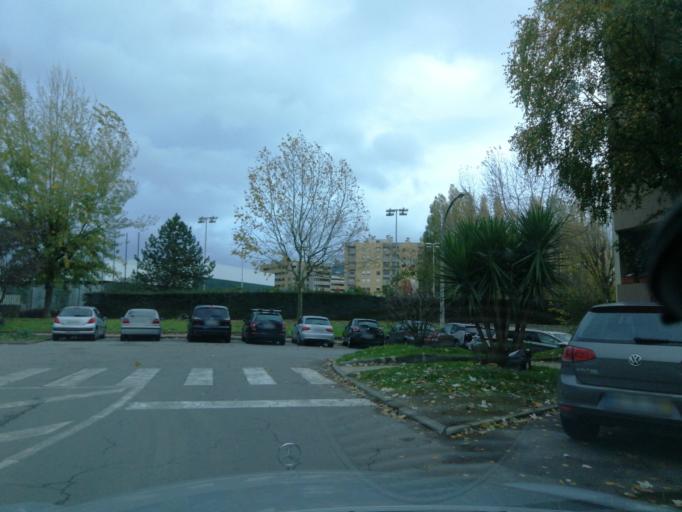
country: PT
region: Braga
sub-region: Braga
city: Braga
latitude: 41.5501
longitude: -8.4082
